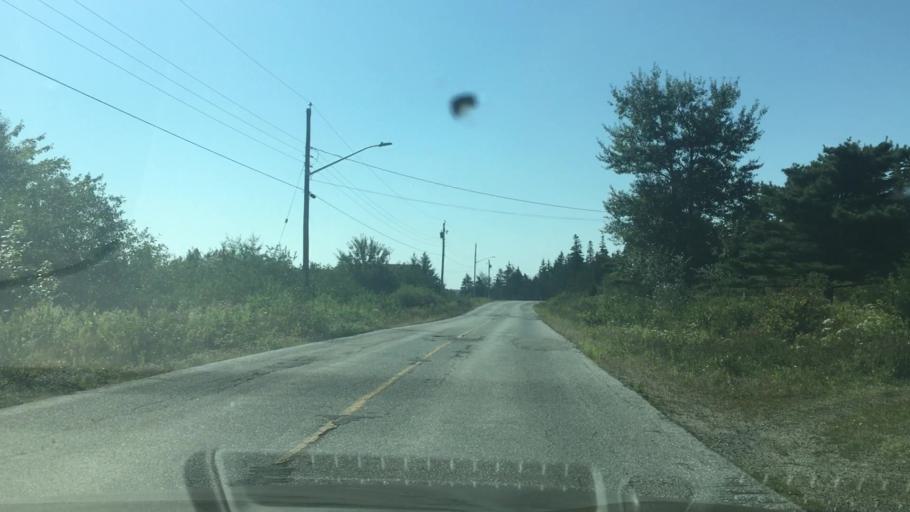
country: CA
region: Nova Scotia
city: New Glasgow
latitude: 44.8037
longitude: -62.6933
